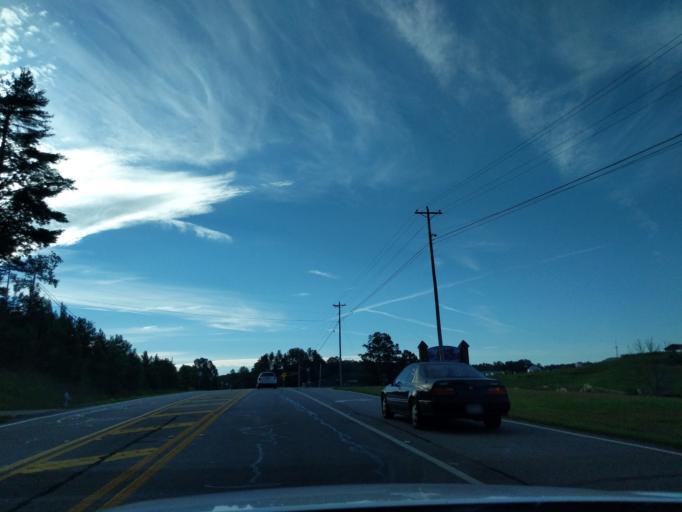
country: US
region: Georgia
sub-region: Fannin County
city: Blue Ridge
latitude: 34.8885
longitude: -84.3438
